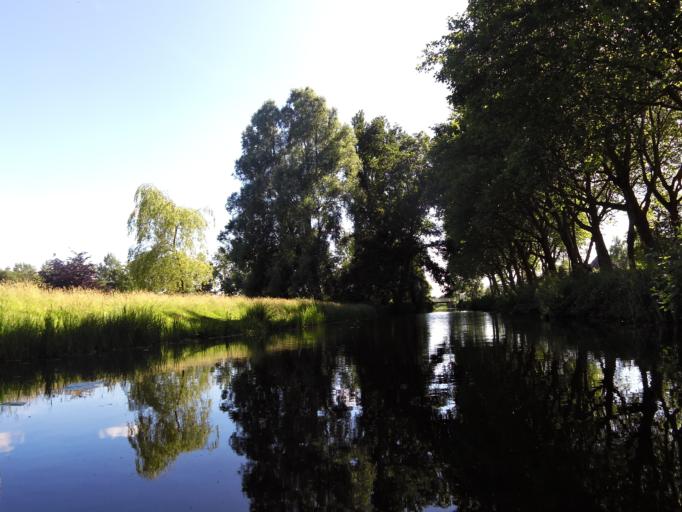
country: NL
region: South Holland
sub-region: Gemeente Wassenaar
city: Wassenaar
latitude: 52.1299
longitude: 4.3841
